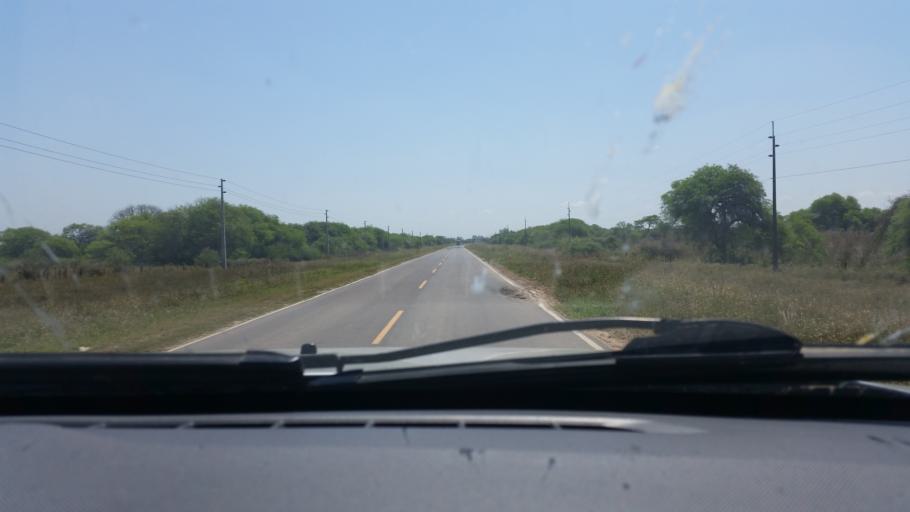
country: PY
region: Boqueron
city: Filadelfia
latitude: -22.4199
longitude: -60.0299
